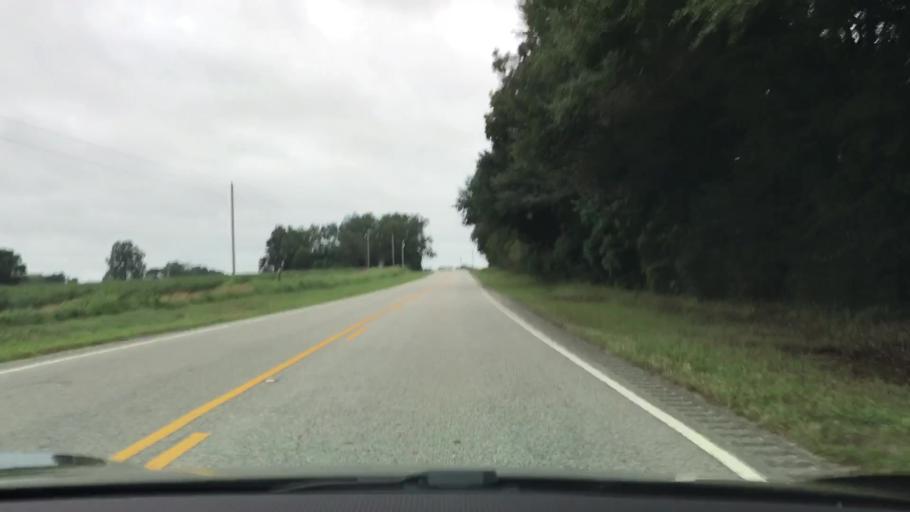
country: US
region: Alabama
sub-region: Coffee County
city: Elba
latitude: 31.3203
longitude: -86.1343
